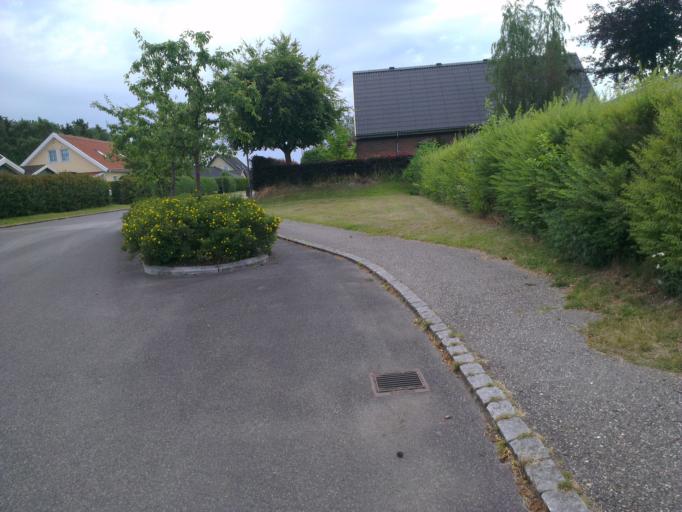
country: DK
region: Capital Region
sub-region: Frederikssund Kommune
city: Skibby
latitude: 55.7432
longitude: 11.9694
